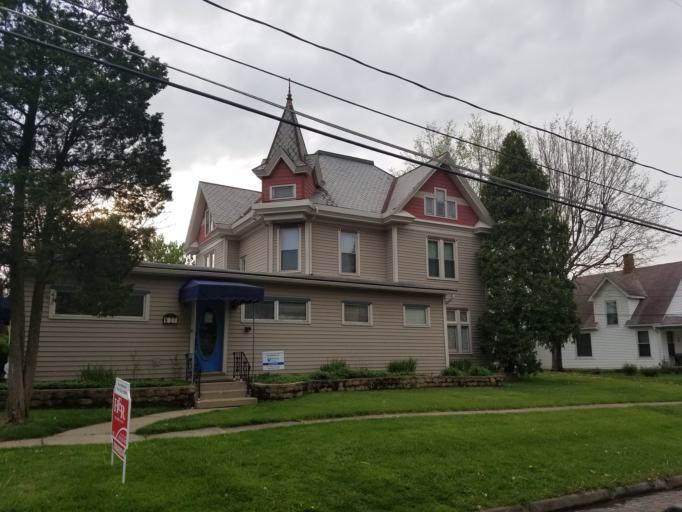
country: US
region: Ohio
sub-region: Delaware County
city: Sunbury
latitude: 40.2430
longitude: -82.8582
